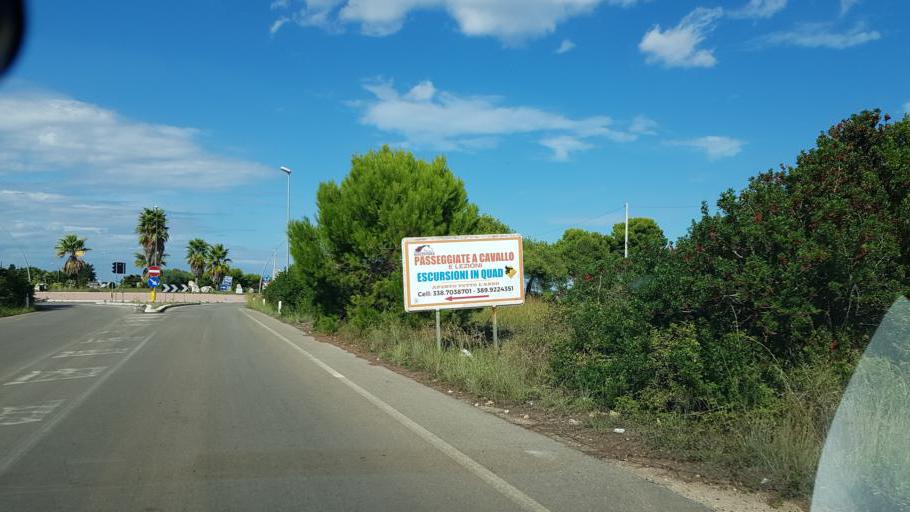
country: IT
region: Apulia
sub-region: Provincia di Lecce
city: Borgagne
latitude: 40.2530
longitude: 18.4391
